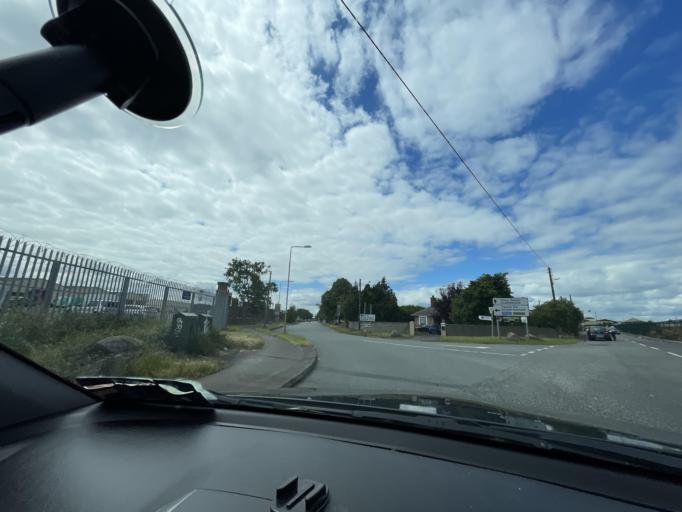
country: IE
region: Leinster
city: Ballyfermot
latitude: 53.3241
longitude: -6.3564
